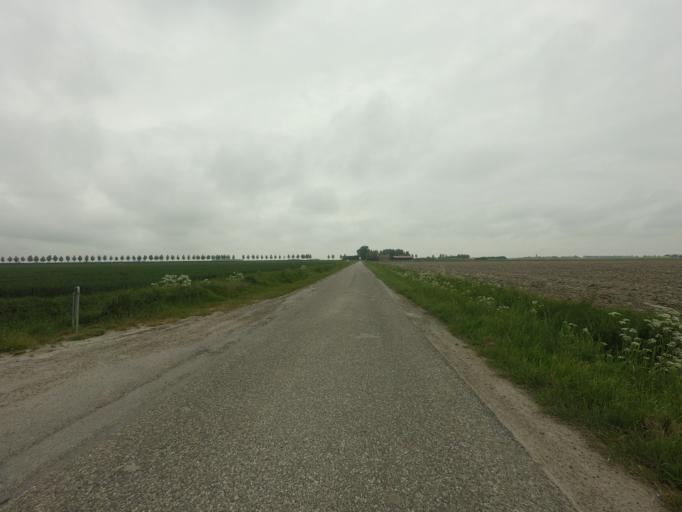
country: NL
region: South Holland
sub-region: Gemeente Goeree-Overflakkee
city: Dirksland
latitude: 51.7206
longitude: 4.1160
